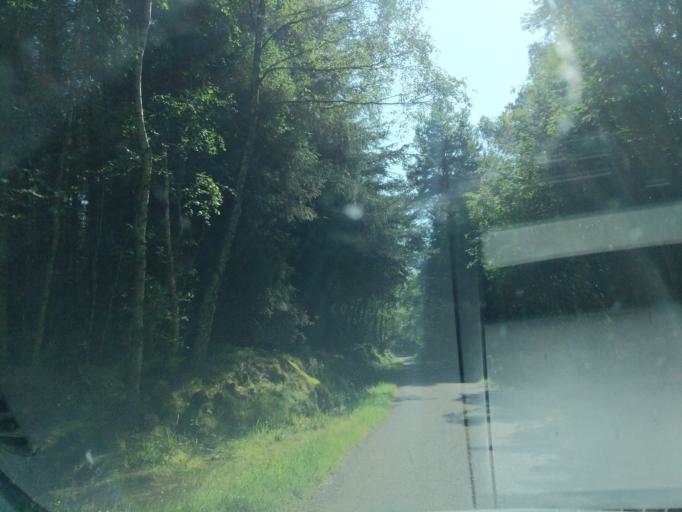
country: GB
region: Scotland
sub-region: Moray
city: Fochabers
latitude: 57.5716
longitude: -3.1202
